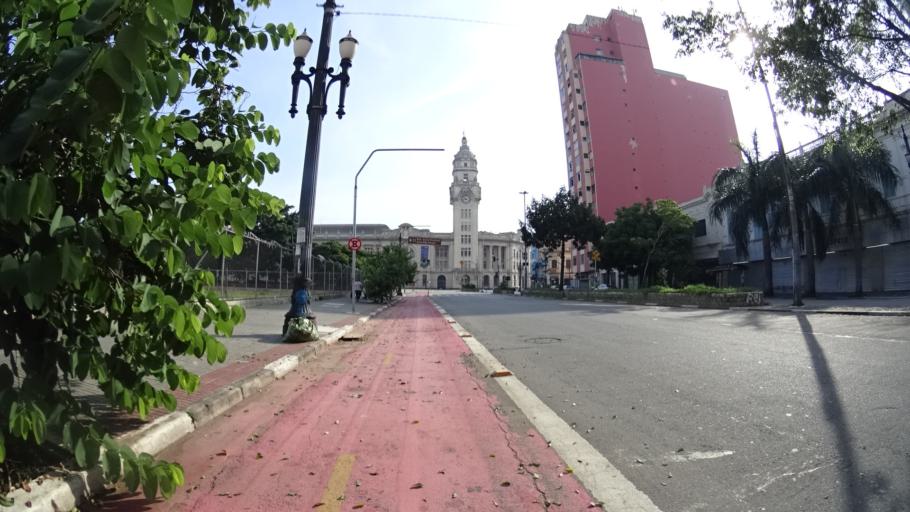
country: BR
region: Sao Paulo
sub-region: Sao Paulo
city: Sao Paulo
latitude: -23.5356
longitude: -46.6414
